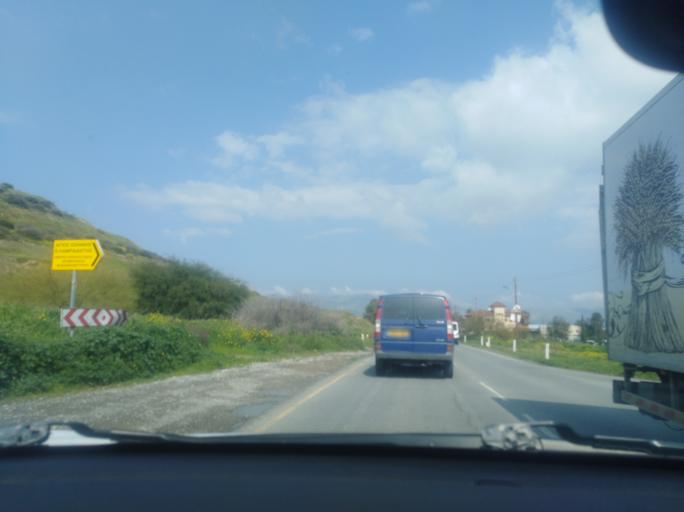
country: CY
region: Lefkosia
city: Nicosia
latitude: 35.1613
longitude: 33.3985
